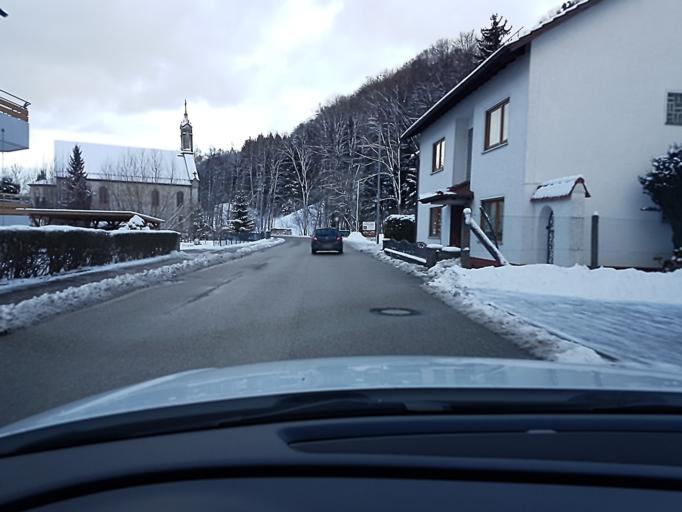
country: DE
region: Baden-Wuerttemberg
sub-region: Regierungsbezirk Stuttgart
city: Spiegelberg
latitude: 49.0591
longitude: 9.4332
